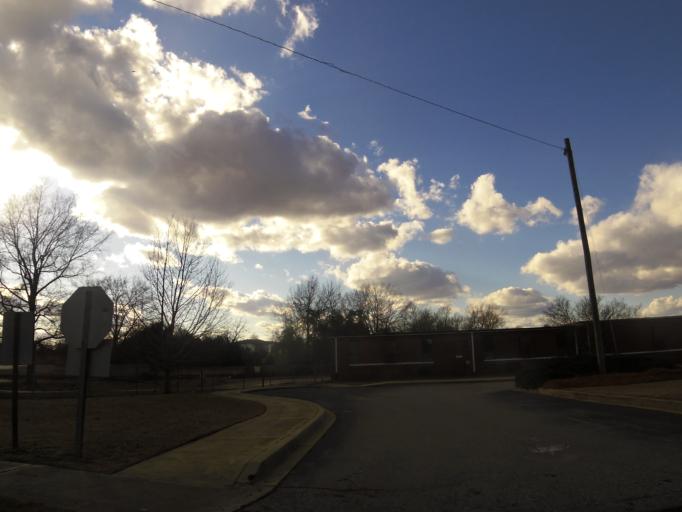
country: US
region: South Carolina
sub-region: Clarendon County
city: Manning
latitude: 33.6974
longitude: -80.2136
